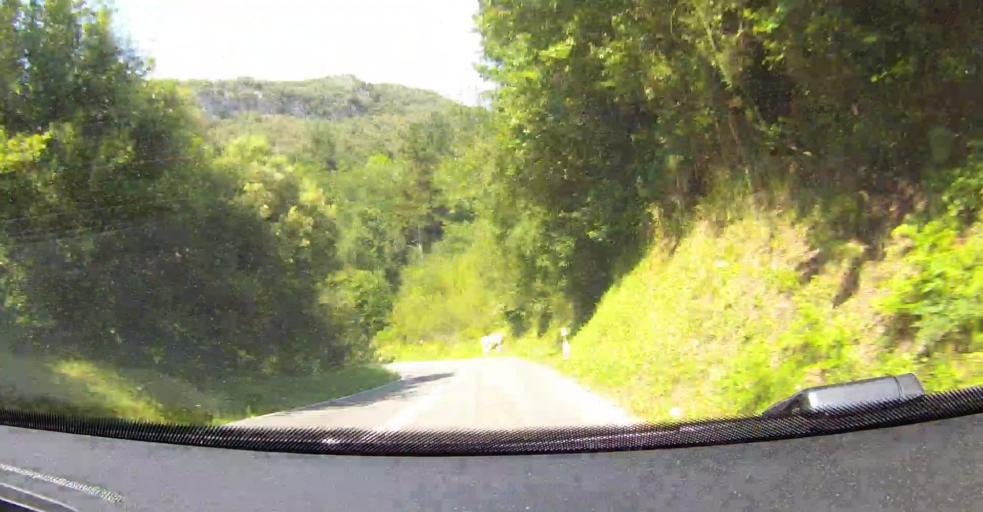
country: ES
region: Basque Country
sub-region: Bizkaia
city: Kortezubi
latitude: 43.3601
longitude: -2.6485
